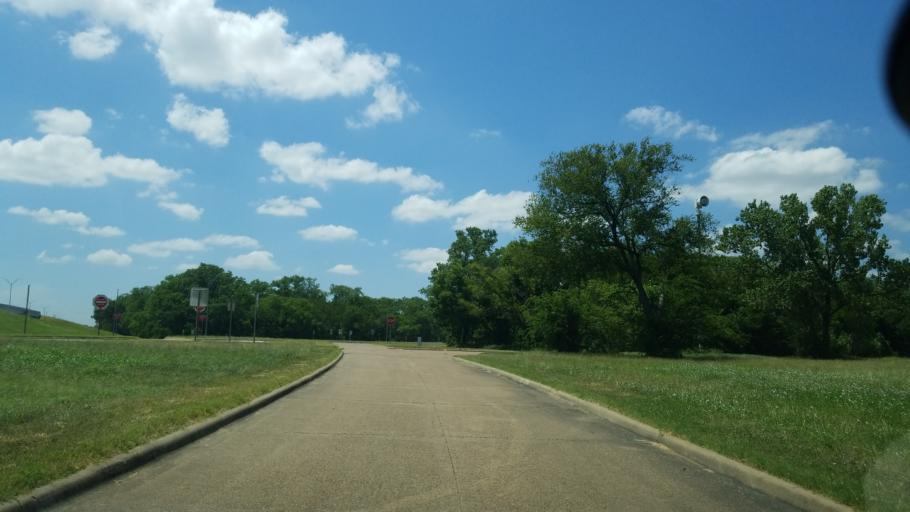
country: US
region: Texas
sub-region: Dallas County
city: Dallas
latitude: 32.7452
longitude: -96.7255
